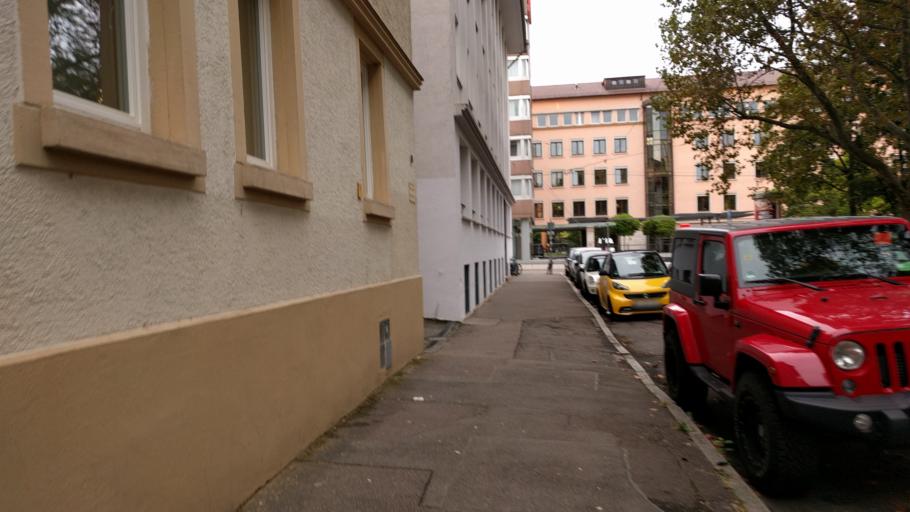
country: DE
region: Baden-Wuerttemberg
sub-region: Regierungsbezirk Stuttgart
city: Stuttgart
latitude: 48.7729
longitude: 9.1637
